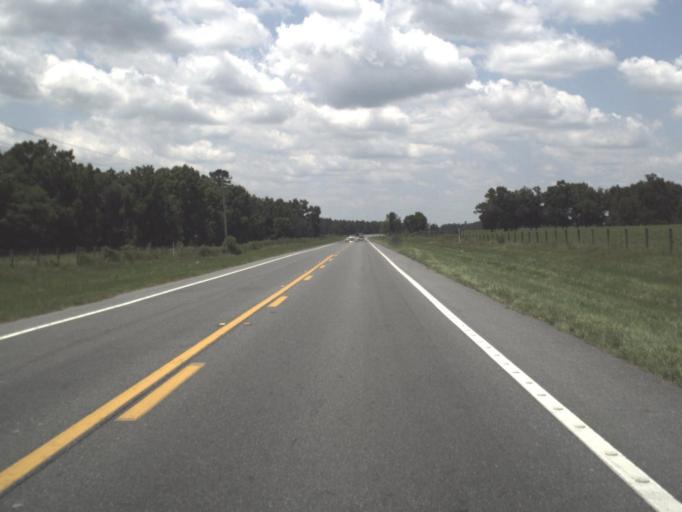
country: US
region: Florida
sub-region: Levy County
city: Williston
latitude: 29.4587
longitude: -82.4122
